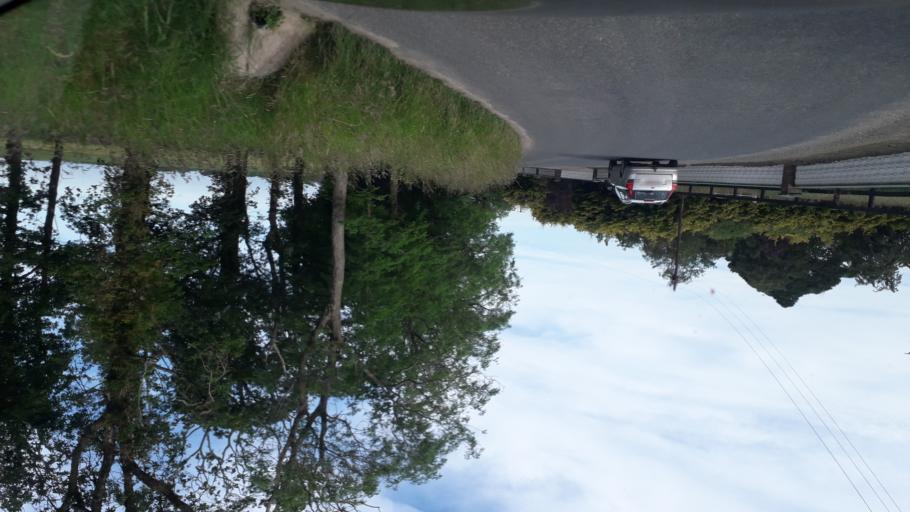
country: IE
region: Leinster
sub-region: Loch Garman
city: Courtown
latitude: 52.5381
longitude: -6.2552
